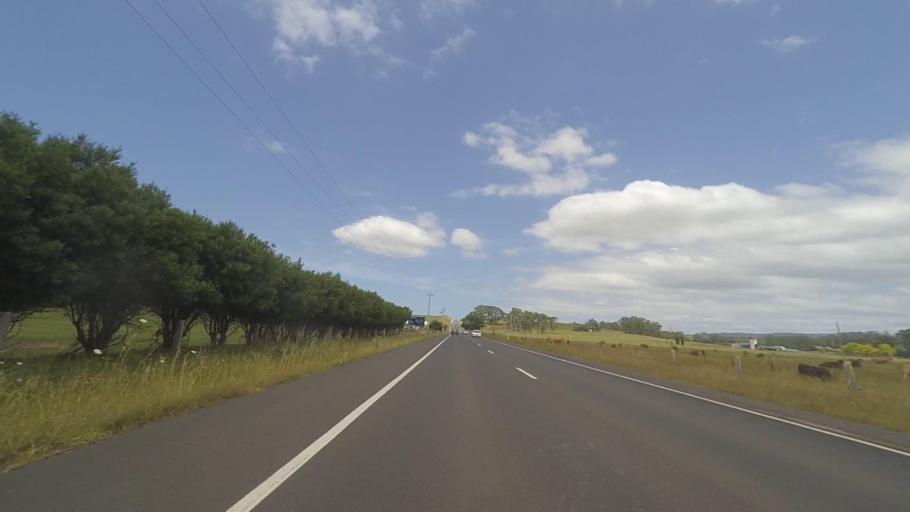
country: AU
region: New South Wales
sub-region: Shoalhaven Shire
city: Milton
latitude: -35.2792
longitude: 150.4229
